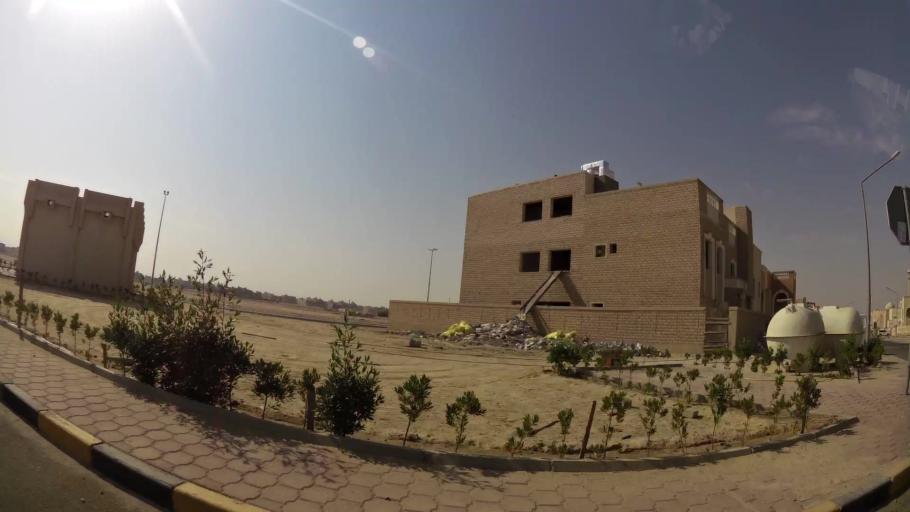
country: KW
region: Al Ahmadi
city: Al Wafrah
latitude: 28.7899
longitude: 48.0740
